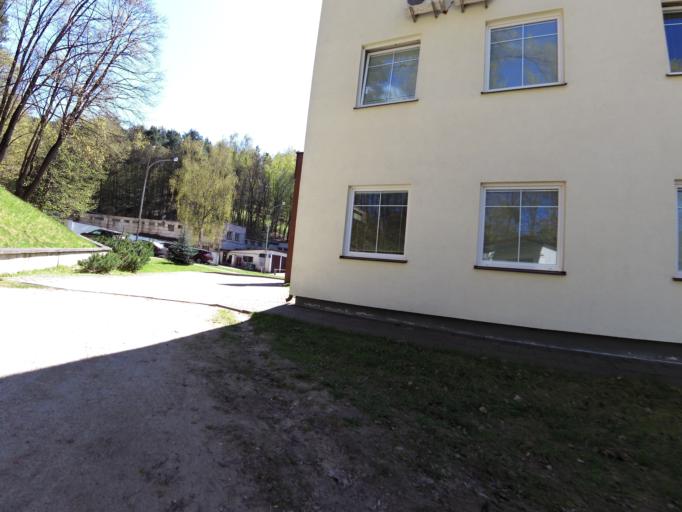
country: LT
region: Vilnius County
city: Rasos
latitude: 54.6905
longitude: 25.3088
